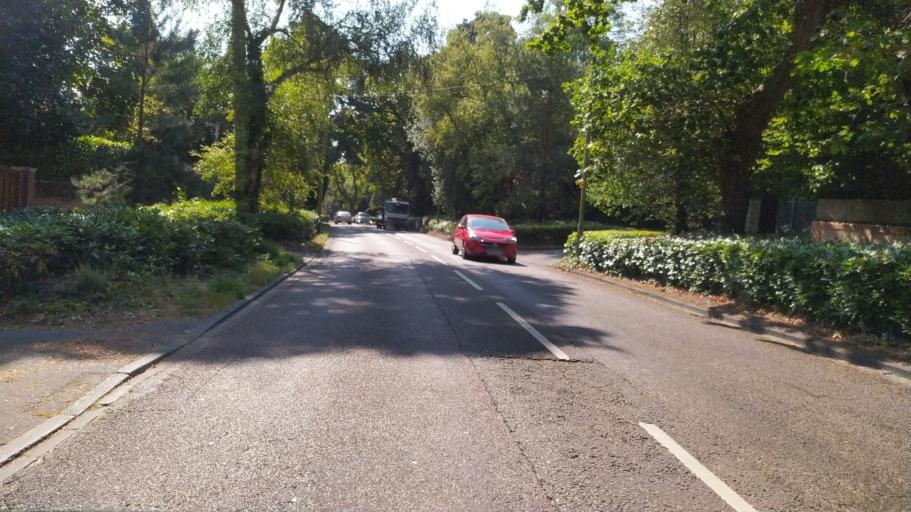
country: GB
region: England
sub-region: Bournemouth
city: Bournemouth
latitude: 50.7119
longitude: -1.9096
